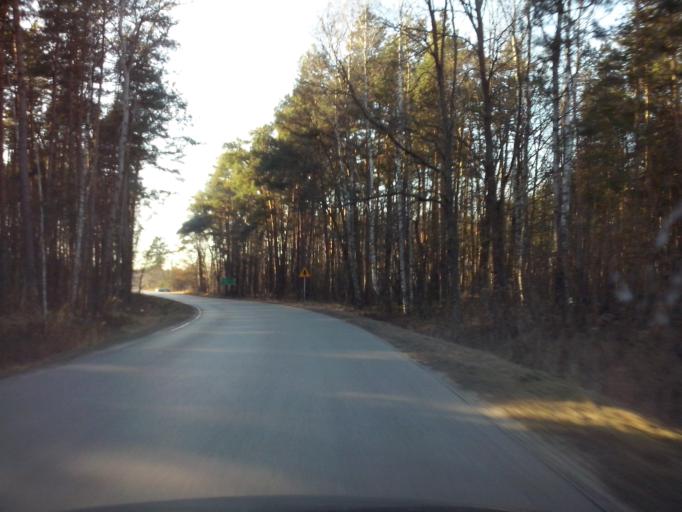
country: PL
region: Subcarpathian Voivodeship
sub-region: Powiat nizanski
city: Harasiuki
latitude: 50.5176
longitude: 22.4566
